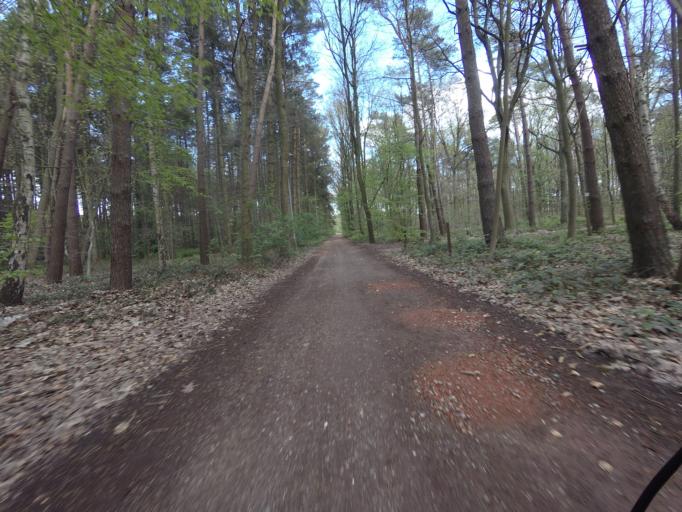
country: BE
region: Flanders
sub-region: Provincie Vlaams-Brabant
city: Kampenhout
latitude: 50.9765
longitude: 4.5259
